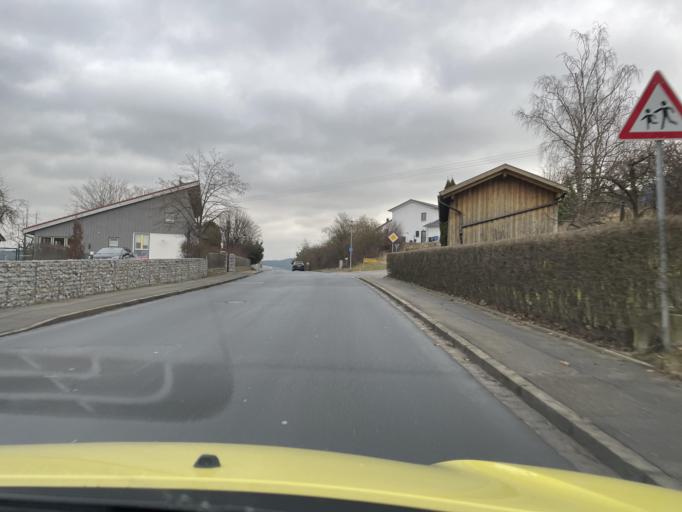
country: DE
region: Bavaria
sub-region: Upper Palatinate
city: Traitsching
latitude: 49.1751
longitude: 12.6816
